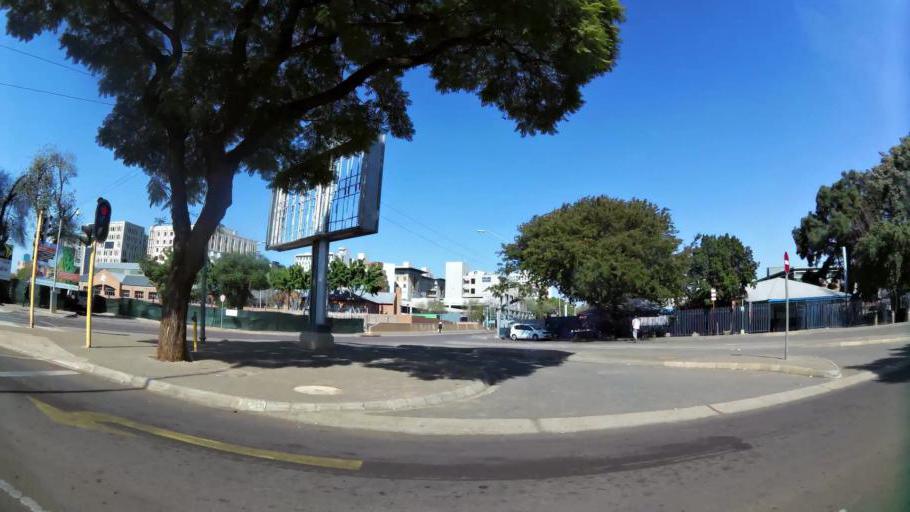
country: ZA
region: Gauteng
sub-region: City of Tshwane Metropolitan Municipality
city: Pretoria
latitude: -25.7488
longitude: 28.2324
